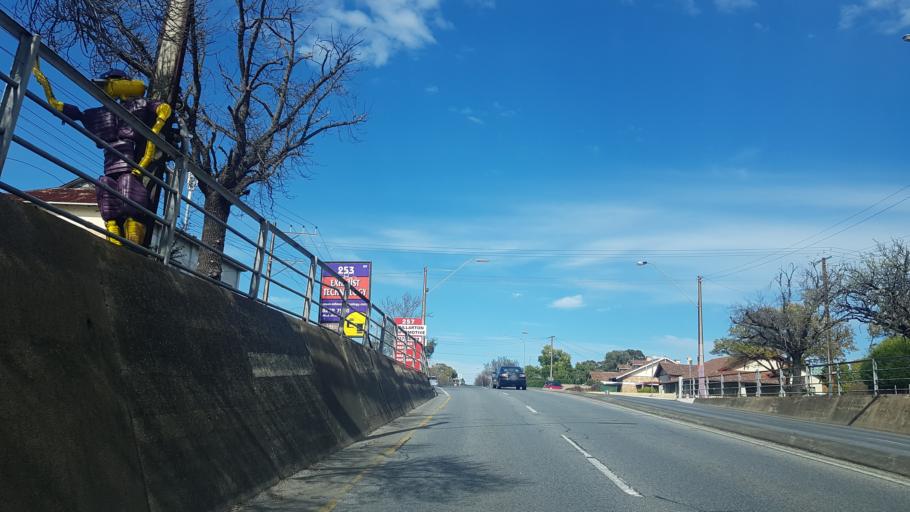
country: AU
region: South Australia
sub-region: Unley
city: Millswood
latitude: -34.9591
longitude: 138.5902
